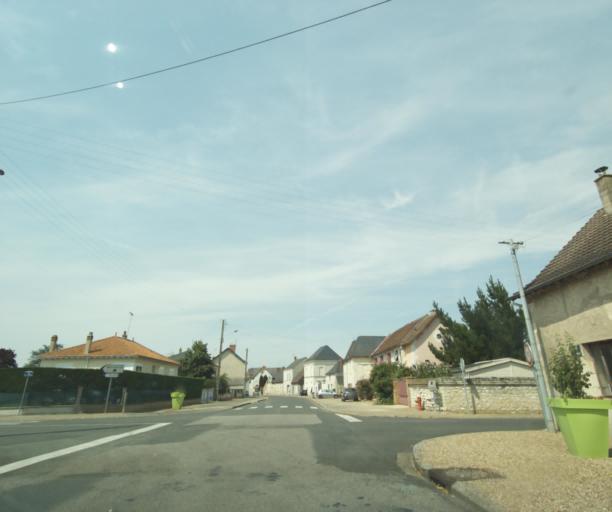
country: FR
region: Centre
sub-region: Departement d'Indre-et-Loire
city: La Celle-Saint-Avant
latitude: 47.0014
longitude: 0.6002
